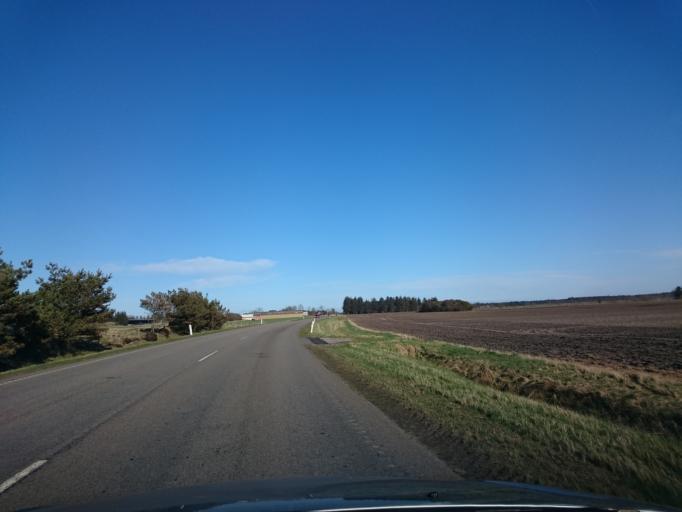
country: DK
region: North Denmark
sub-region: Hjorring Kommune
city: Sindal
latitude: 57.6060
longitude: 10.3372
